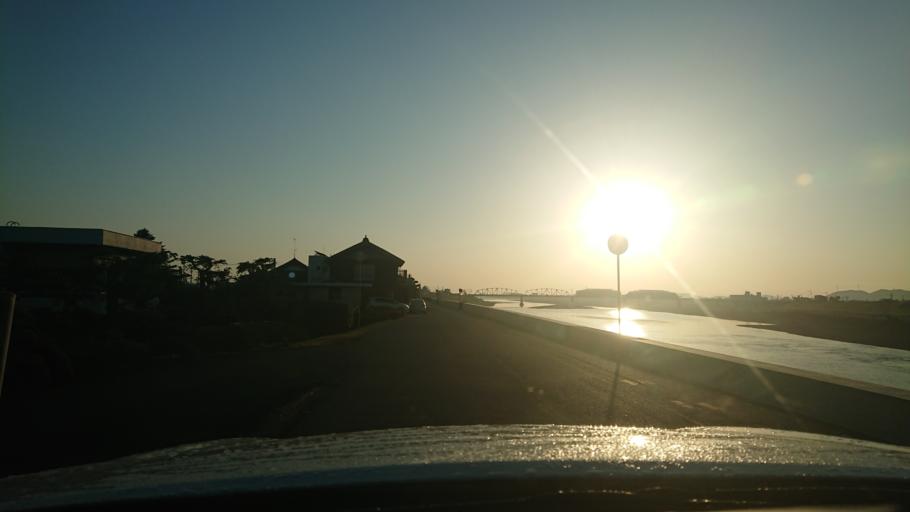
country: JP
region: Tokushima
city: Anan
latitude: 33.9411
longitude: 134.6140
